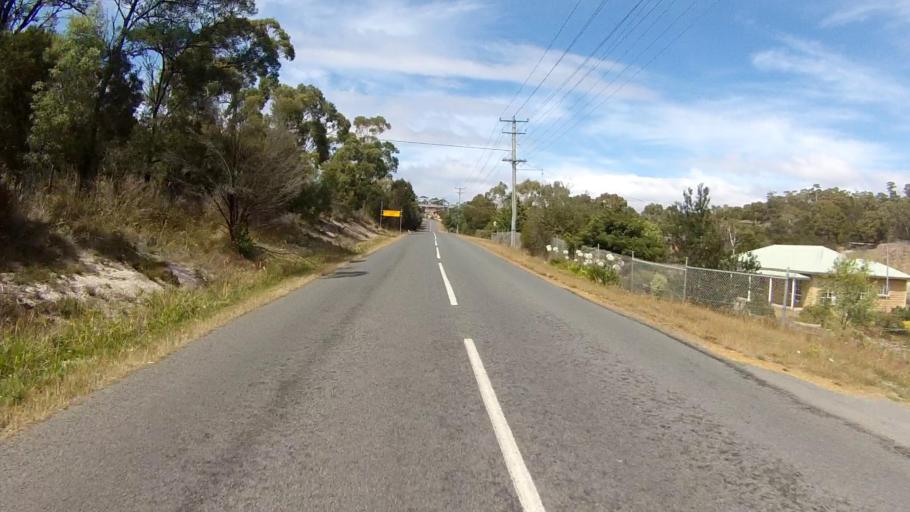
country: AU
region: Tasmania
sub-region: Clarence
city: Lindisfarne
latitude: -42.8177
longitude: 147.3513
